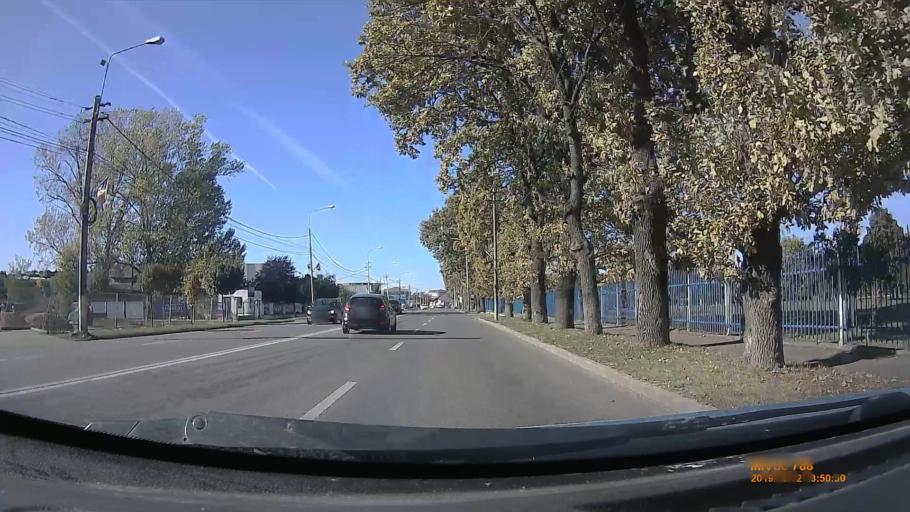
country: RO
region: Bihor
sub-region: Comuna Sanmartin
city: Sanmartin
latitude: 47.0424
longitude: 21.9737
